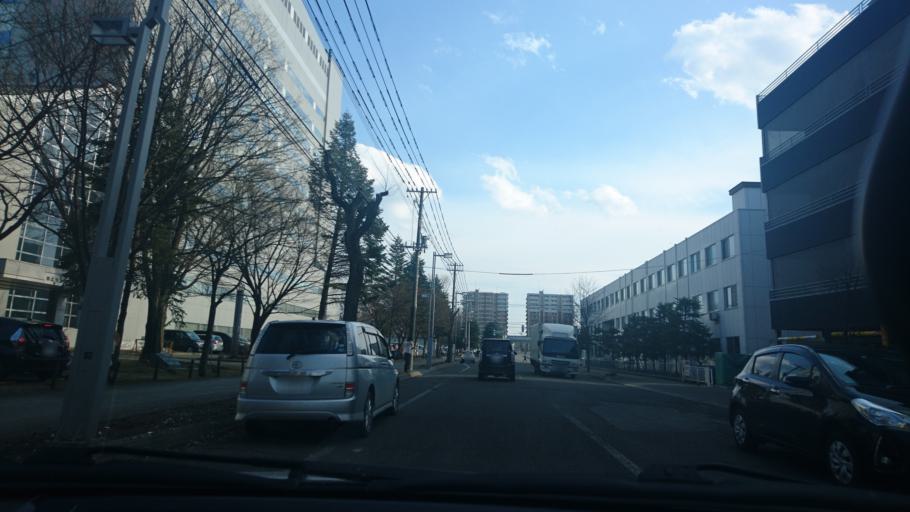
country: JP
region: Hokkaido
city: Obihiro
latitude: 42.9243
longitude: 143.1956
